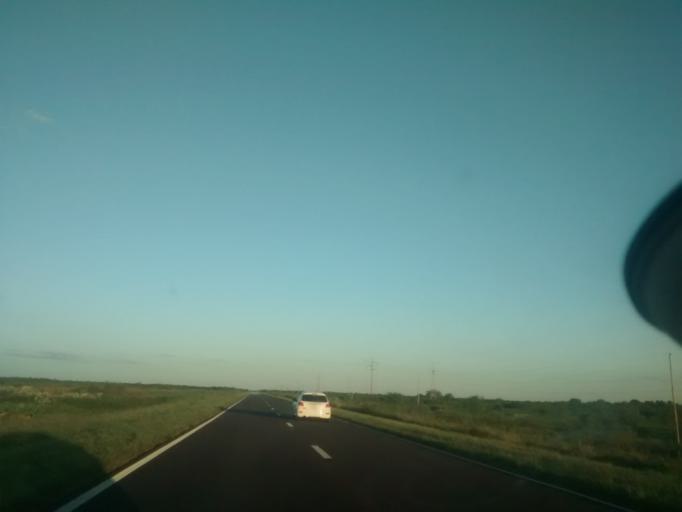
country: AR
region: Chaco
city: La Escondida
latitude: -27.0969
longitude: -59.6173
